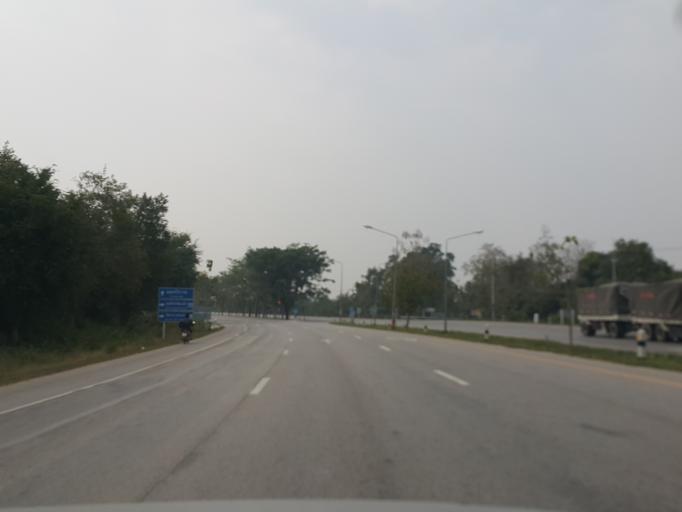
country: TH
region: Lampang
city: Ko Kha
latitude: 18.1447
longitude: 99.3931
